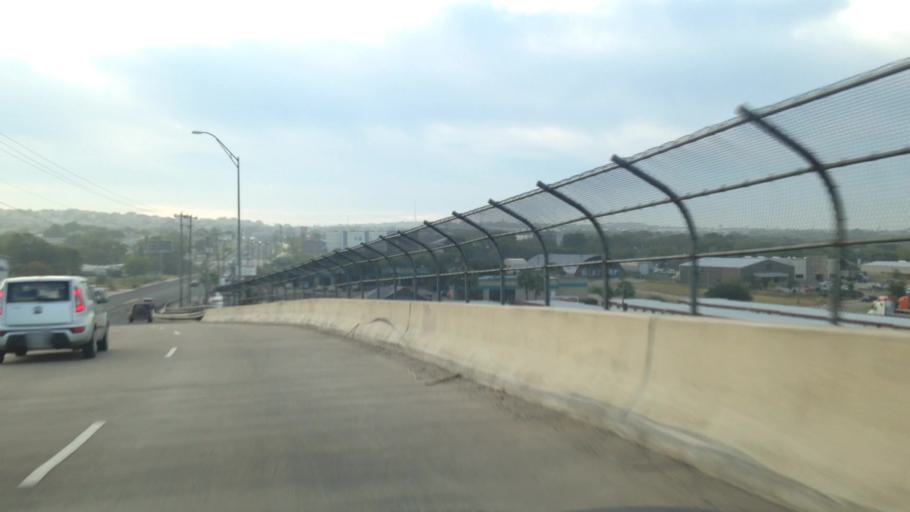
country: US
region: Texas
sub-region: Bexar County
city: Live Oak
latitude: 29.5670
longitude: -98.3657
